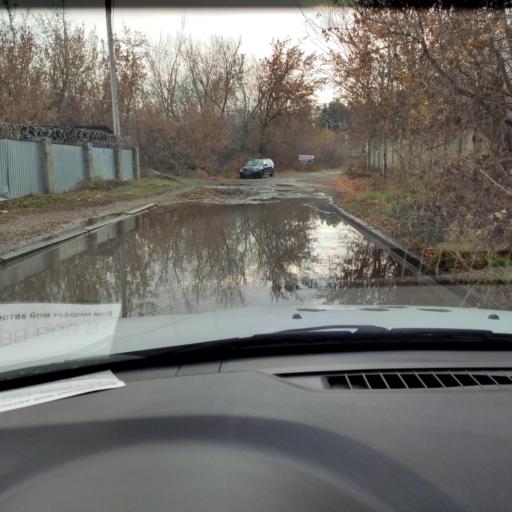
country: RU
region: Samara
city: Tol'yatti
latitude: 53.5273
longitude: 49.3915
